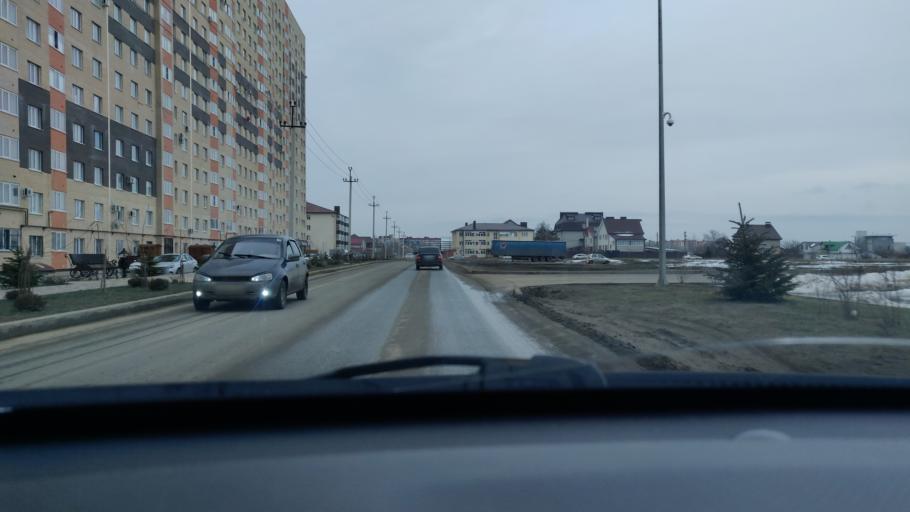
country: RU
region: Stavropol'skiy
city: Tatarka
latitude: 45.0099
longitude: 41.9014
